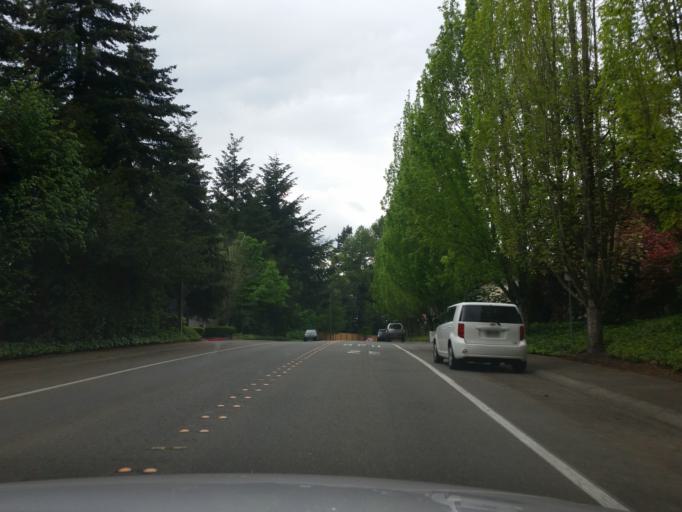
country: US
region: Washington
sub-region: King County
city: Yarrow Point
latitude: 47.6428
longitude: -122.1878
